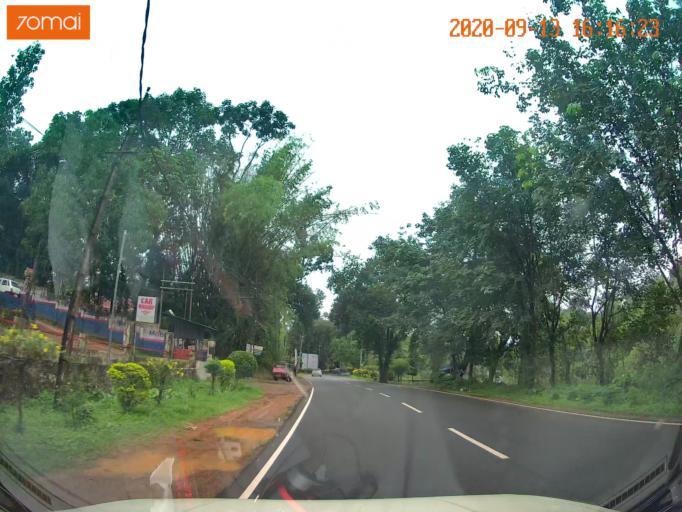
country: IN
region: Kerala
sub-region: Kottayam
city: Palackattumala
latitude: 9.6968
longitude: 76.6476
